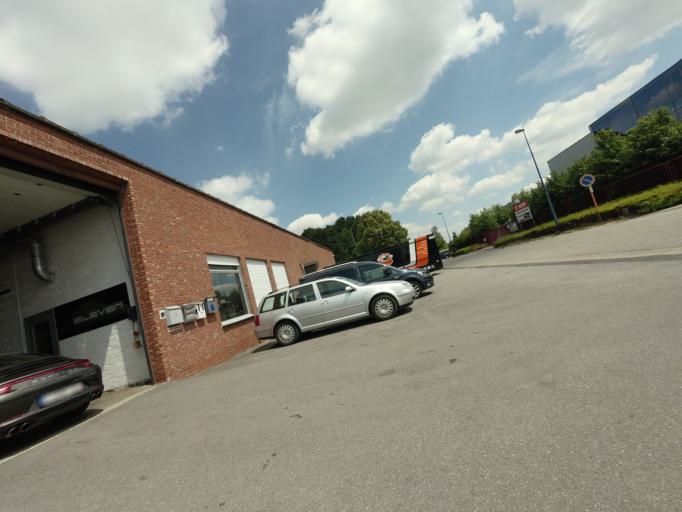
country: BE
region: Flanders
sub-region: Provincie Antwerpen
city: Kontich
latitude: 51.1236
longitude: 4.4528
